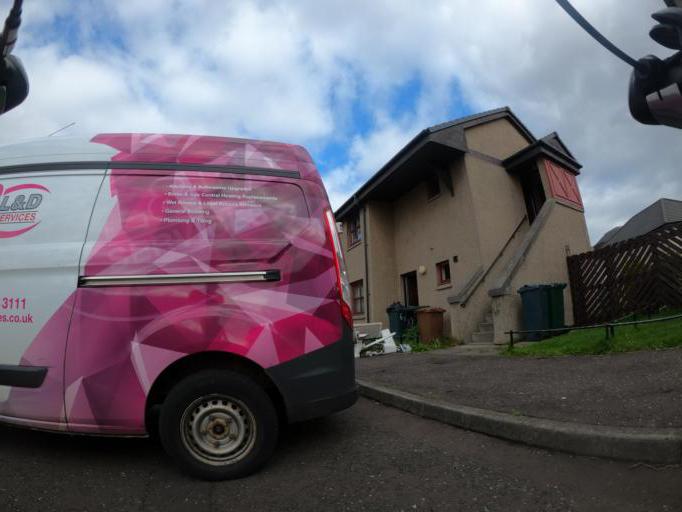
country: GB
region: Scotland
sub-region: Edinburgh
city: Colinton
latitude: 55.9680
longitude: -3.2577
